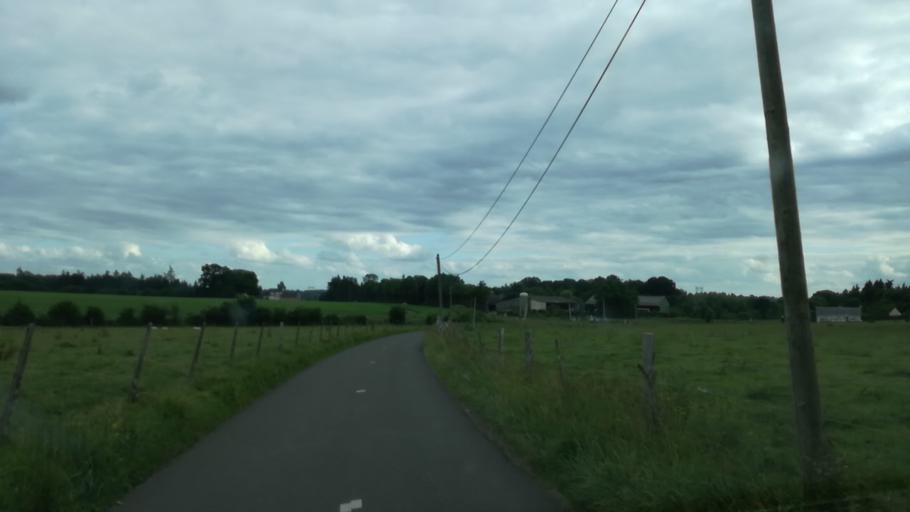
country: FR
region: Haute-Normandie
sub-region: Departement de l'Eure
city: Bourg-Achard
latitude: 49.2977
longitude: 0.8049
